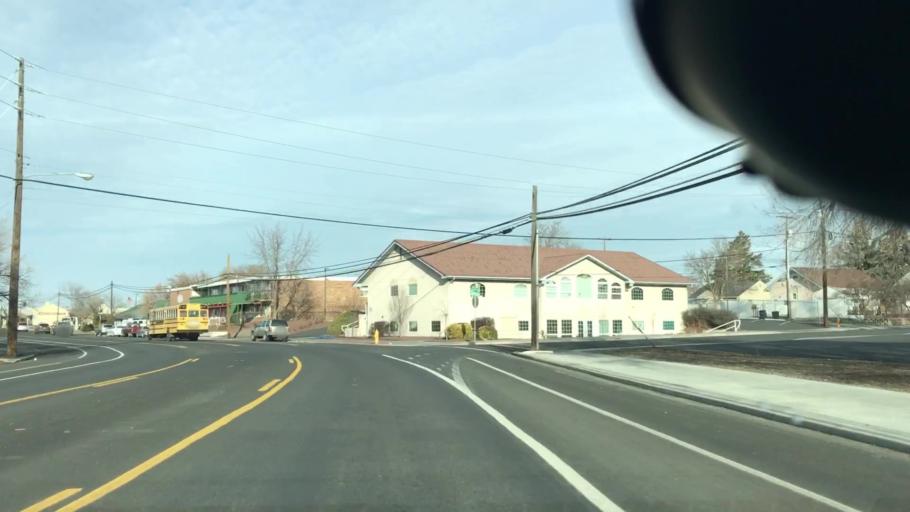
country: US
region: Washington
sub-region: Grant County
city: Moses Lake
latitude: 47.1265
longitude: -119.2745
